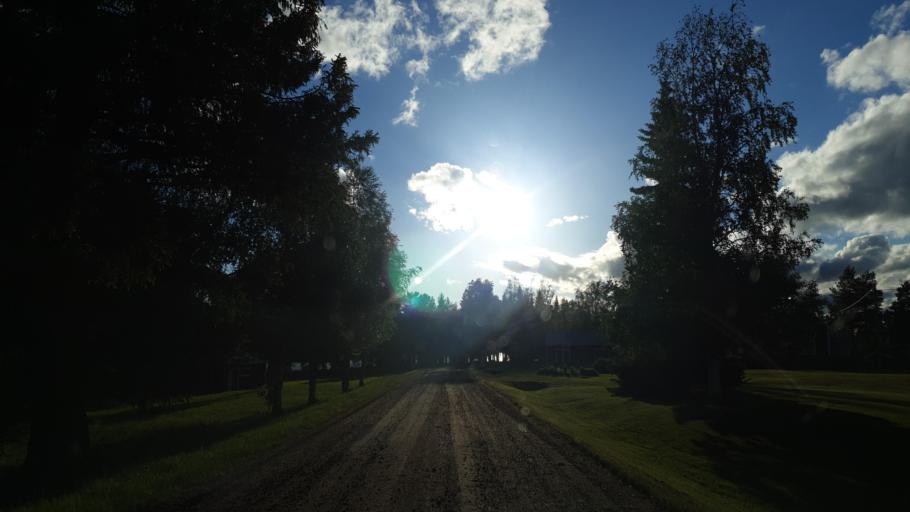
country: SE
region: Norrbotten
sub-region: Arvidsjaurs Kommun
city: Arvidsjaur
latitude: 65.7079
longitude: 18.7086
